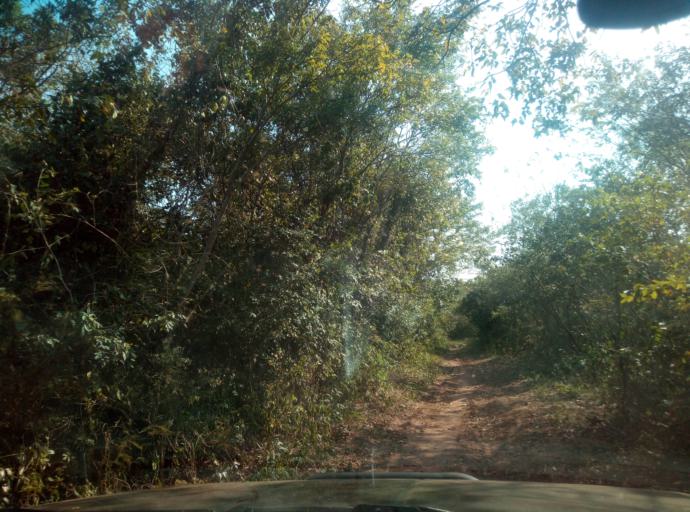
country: PY
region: Caaguazu
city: San Joaquin
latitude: -25.1565
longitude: -56.1234
